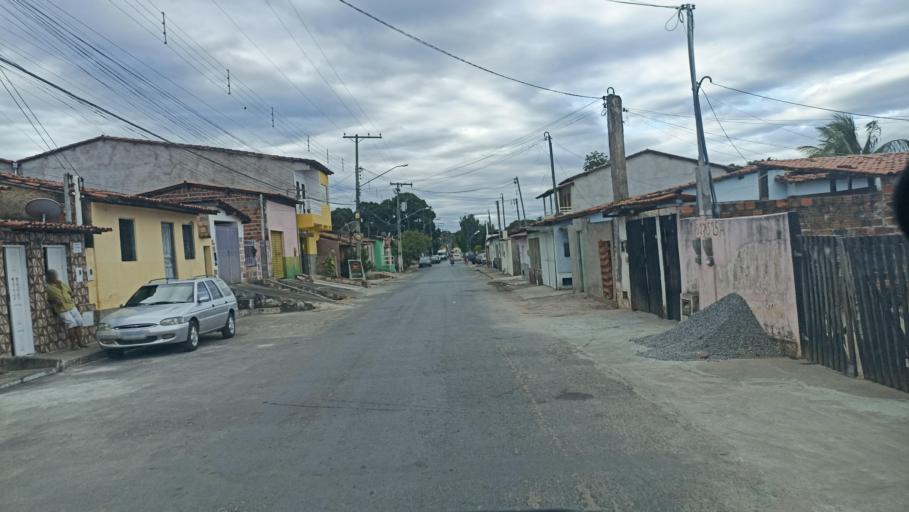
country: BR
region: Bahia
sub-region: Andarai
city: Vera Cruz
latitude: -12.8148
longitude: -41.3318
